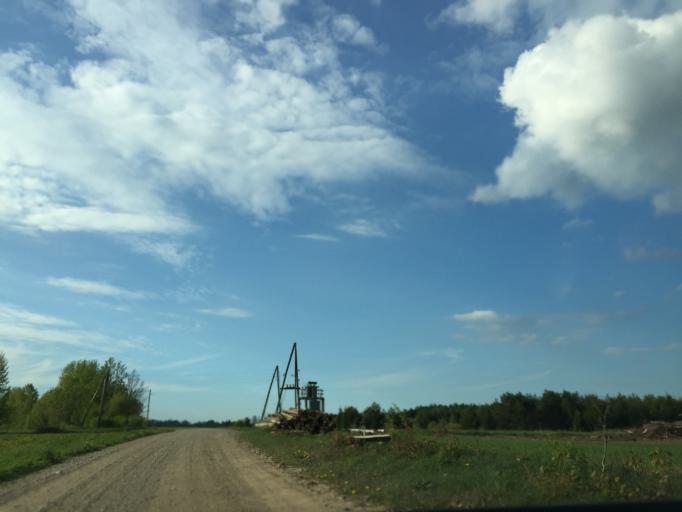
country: LV
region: Limbazu Rajons
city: Limbazi
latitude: 57.3617
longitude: 24.6968
